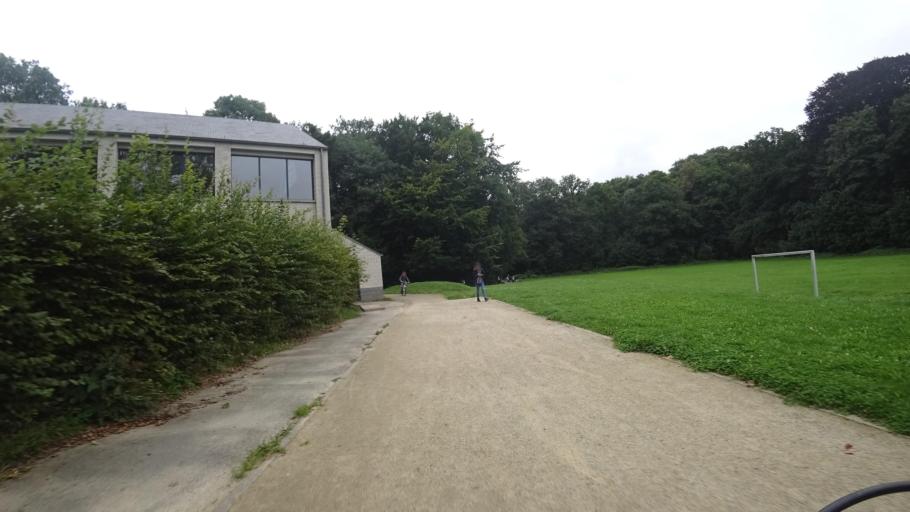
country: BE
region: Wallonia
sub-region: Province du Brabant Wallon
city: Mont-Saint-Guibert
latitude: 50.6376
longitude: 4.6037
